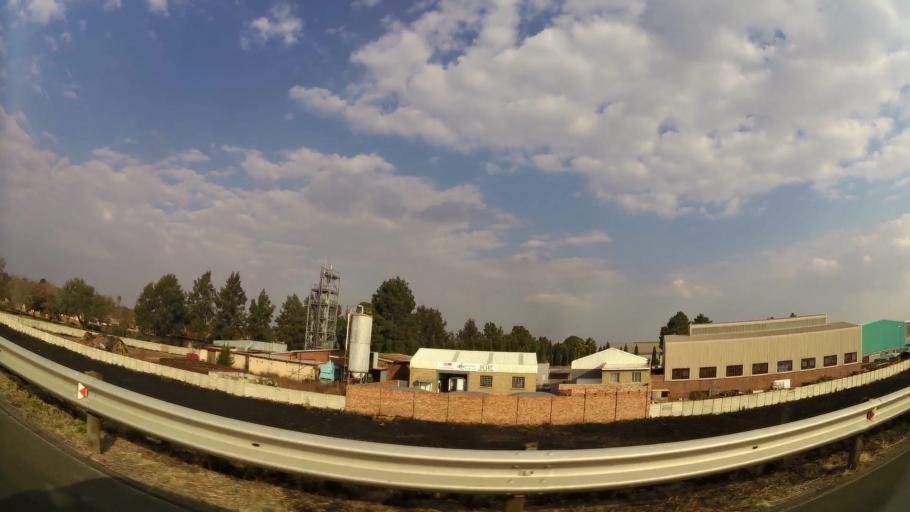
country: ZA
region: Gauteng
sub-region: Ekurhuleni Metropolitan Municipality
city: Springs
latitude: -26.2768
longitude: 28.4597
